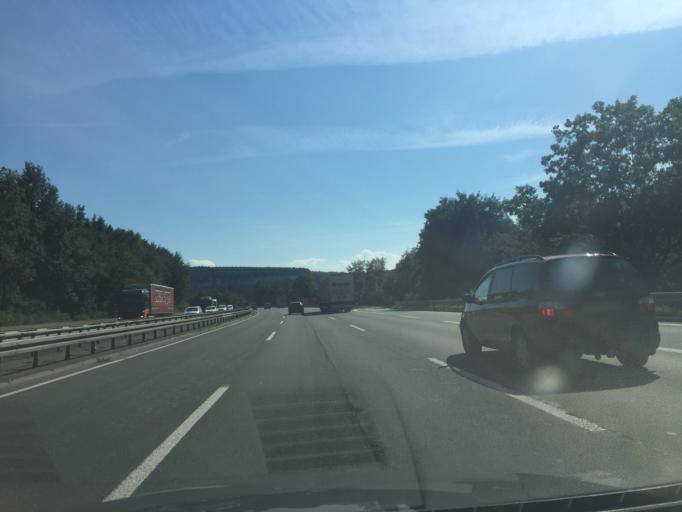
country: DE
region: North Rhine-Westphalia
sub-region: Regierungsbezirk Arnsberg
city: Wilnsdorf
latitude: 50.8008
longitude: 8.0973
